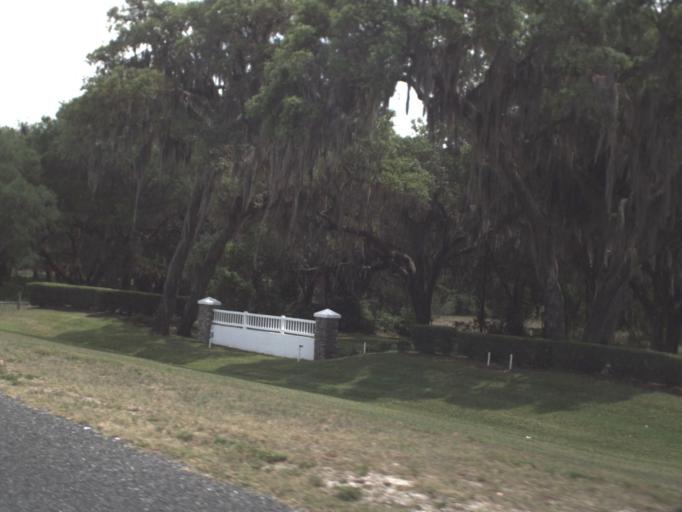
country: US
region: Florida
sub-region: Sumter County
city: Wildwood
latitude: 28.8235
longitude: -81.9861
